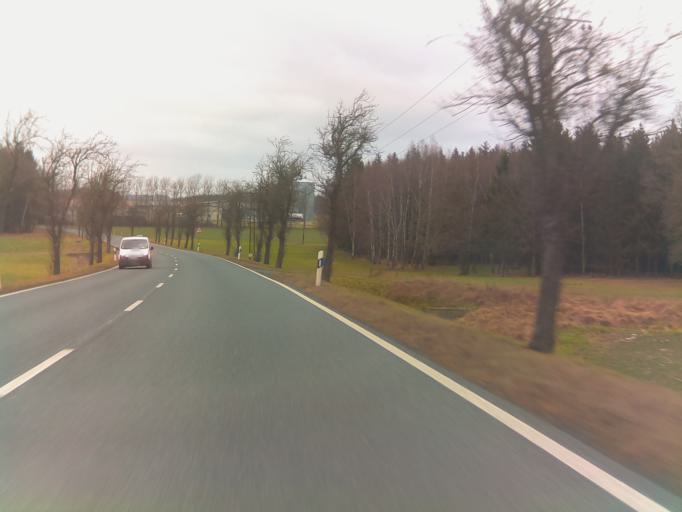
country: DE
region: Thuringia
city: Auma
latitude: 50.6744
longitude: 11.9382
